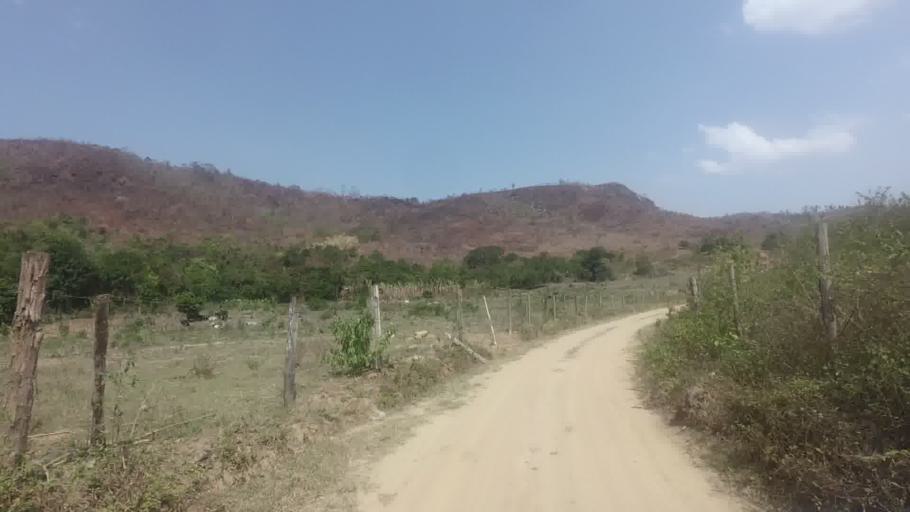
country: BR
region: Espirito Santo
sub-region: Sao Jose Do Calcado
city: Sao Jose do Calcado
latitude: -21.0273
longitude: -41.5168
